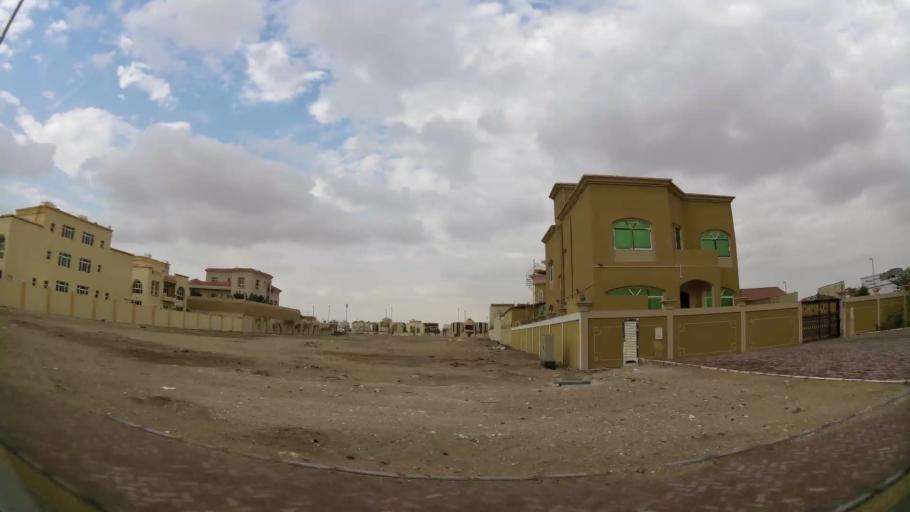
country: AE
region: Abu Dhabi
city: Abu Dhabi
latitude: 24.3529
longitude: 54.6145
